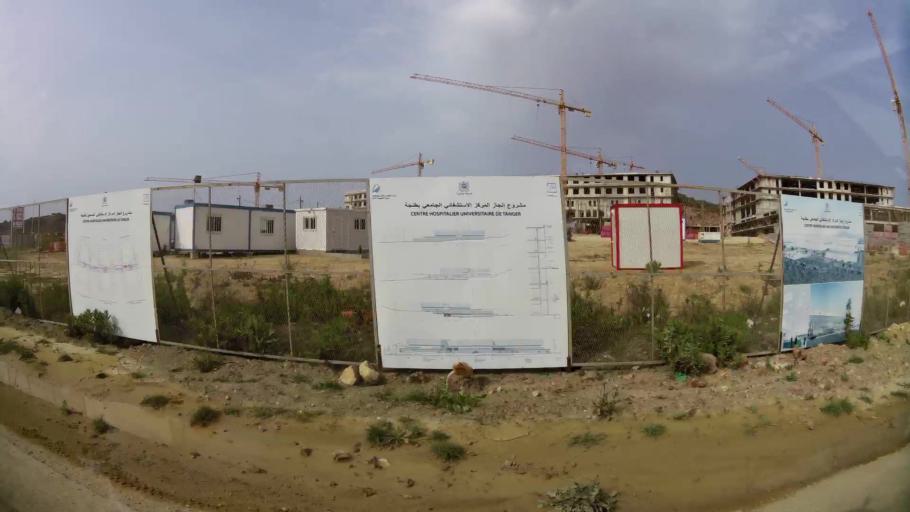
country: MA
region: Tanger-Tetouan
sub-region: Tanger-Assilah
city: Boukhalef
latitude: 35.6821
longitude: -5.9275
